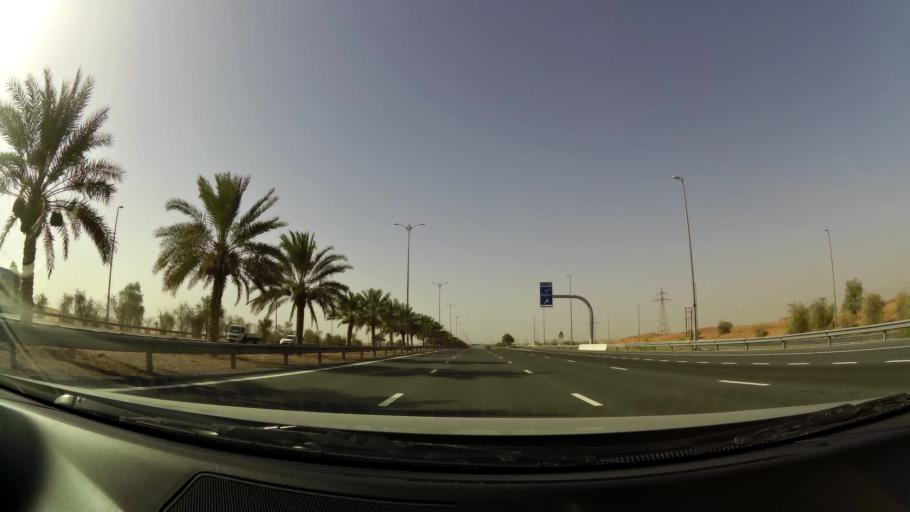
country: OM
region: Al Buraimi
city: Al Buraymi
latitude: 24.4136
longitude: 55.7929
